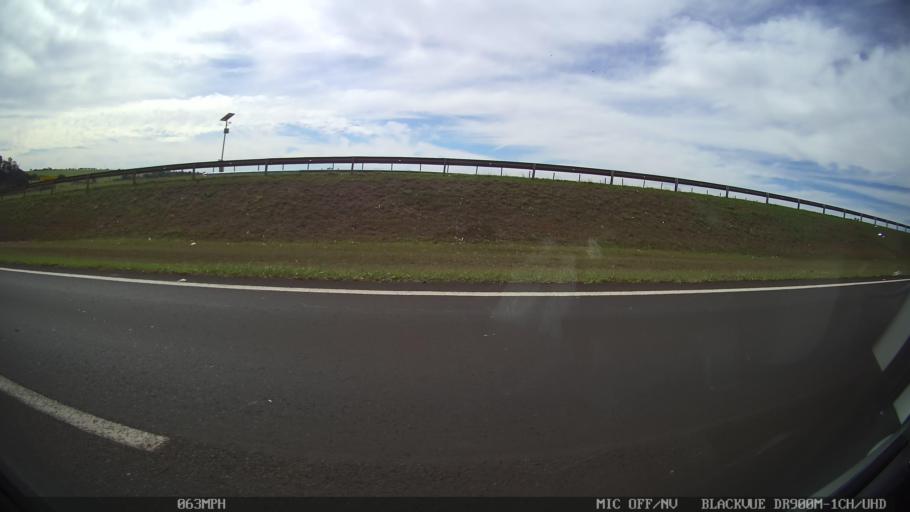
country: BR
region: Sao Paulo
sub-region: Taquaritinga
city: Taquaritinga
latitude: -21.5241
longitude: -48.5279
